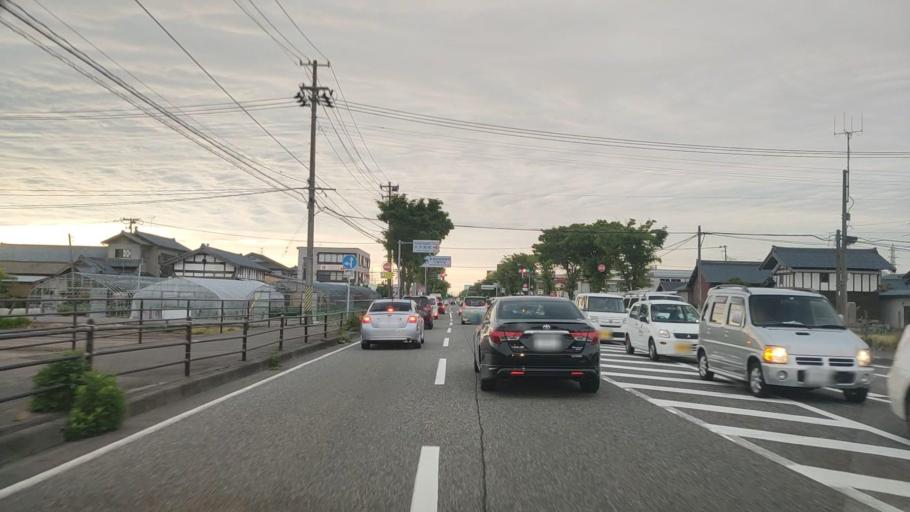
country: JP
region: Niigata
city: Kameda-honcho
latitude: 37.9130
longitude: 139.0974
